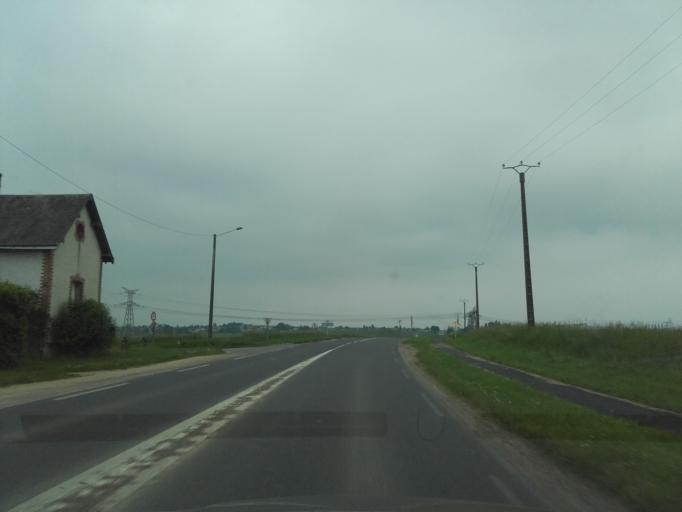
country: FR
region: Centre
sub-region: Departement d'Indre-et-Loire
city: Chanceaux-sur-Choisille
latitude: 47.4879
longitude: 0.6976
